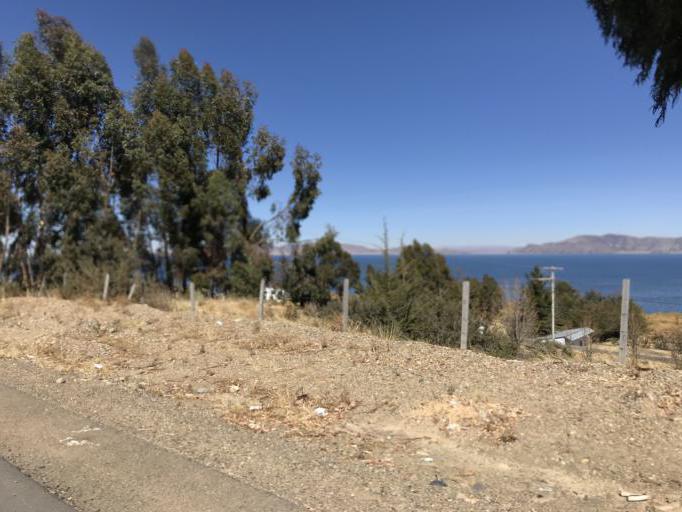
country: BO
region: La Paz
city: Huarina
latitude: -16.2158
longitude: -68.6477
